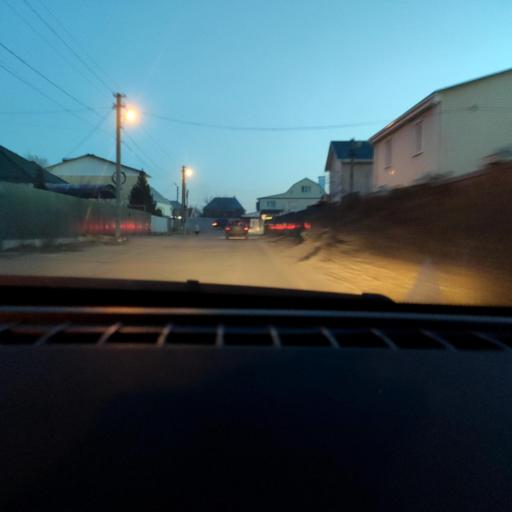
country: RU
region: Voronezj
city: Podgornoye
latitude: 51.7409
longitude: 39.1649
